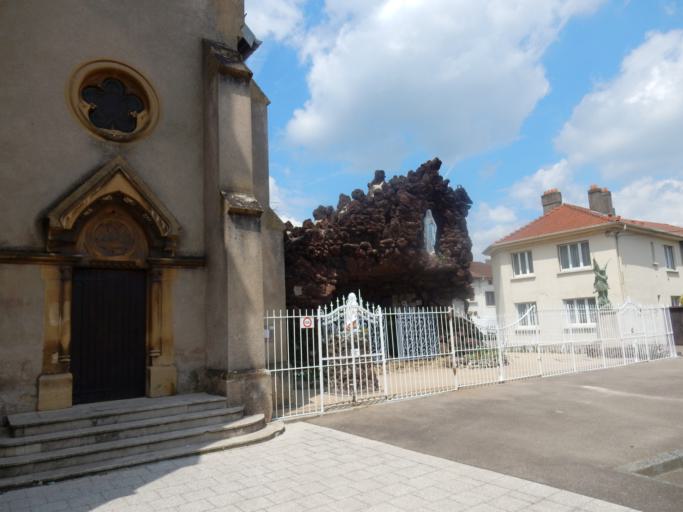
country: FR
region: Lorraine
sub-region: Departement de la Moselle
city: Uckange
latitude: 49.2999
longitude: 6.1600
